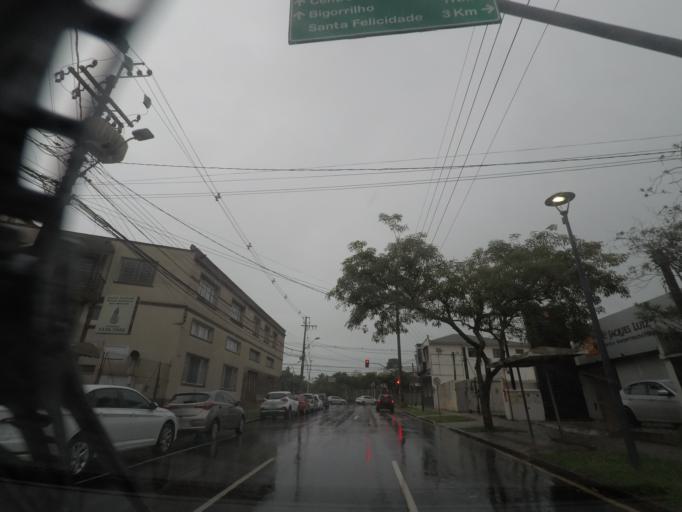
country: BR
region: Parana
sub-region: Curitiba
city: Curitiba
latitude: -25.4219
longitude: -49.2889
